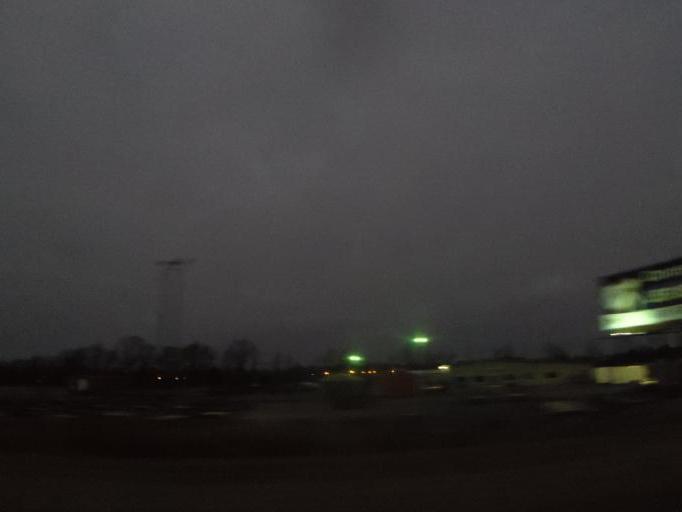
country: US
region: Alabama
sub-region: Morgan County
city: Falkville
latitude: 34.3737
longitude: -86.8922
